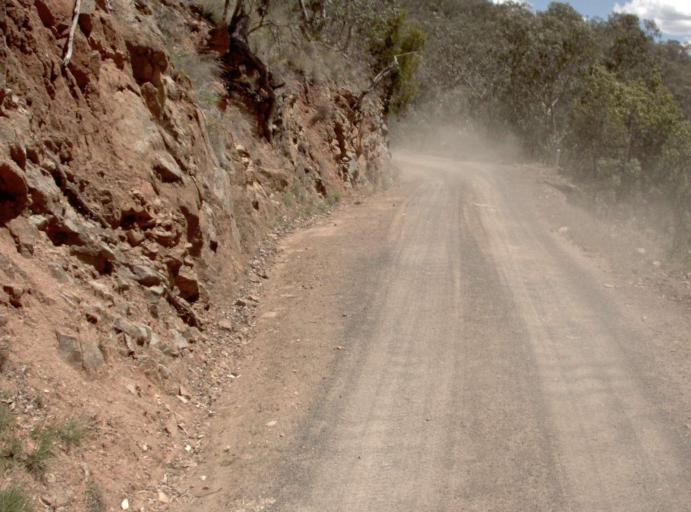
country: AU
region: New South Wales
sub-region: Snowy River
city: Jindabyne
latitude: -37.0845
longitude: 148.4514
